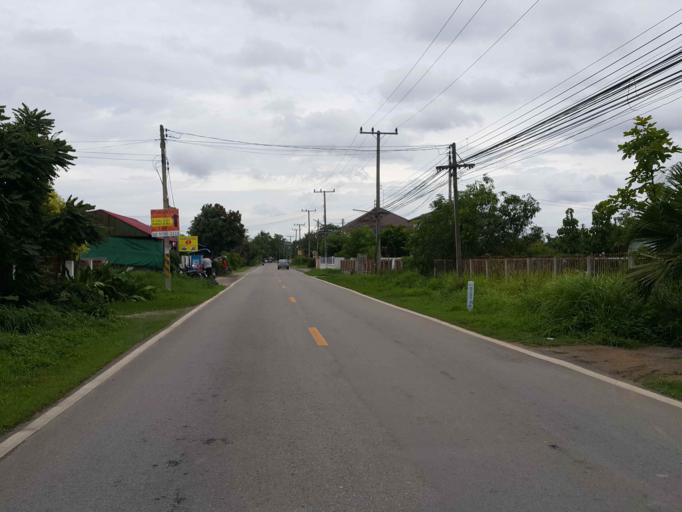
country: TH
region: Chiang Mai
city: San Sai
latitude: 18.8178
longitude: 99.0739
